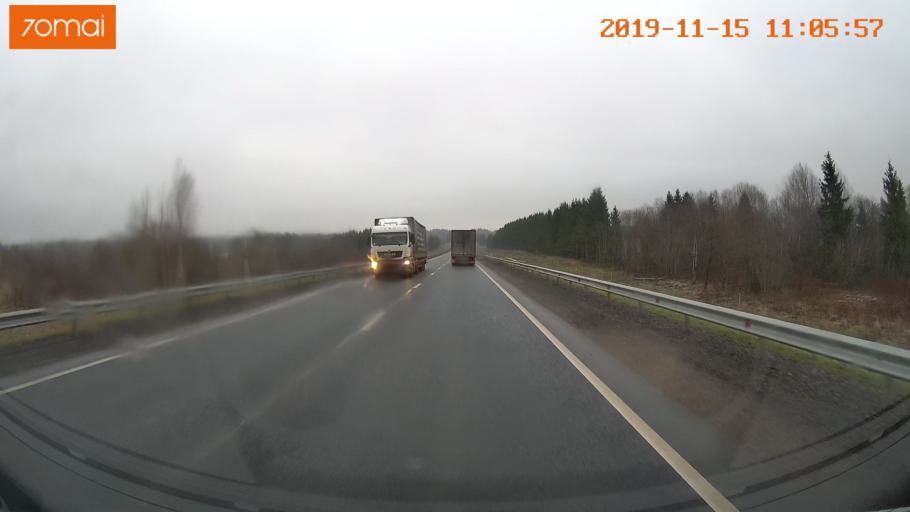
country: RU
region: Vologda
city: Chebsara
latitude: 59.1187
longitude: 39.0165
